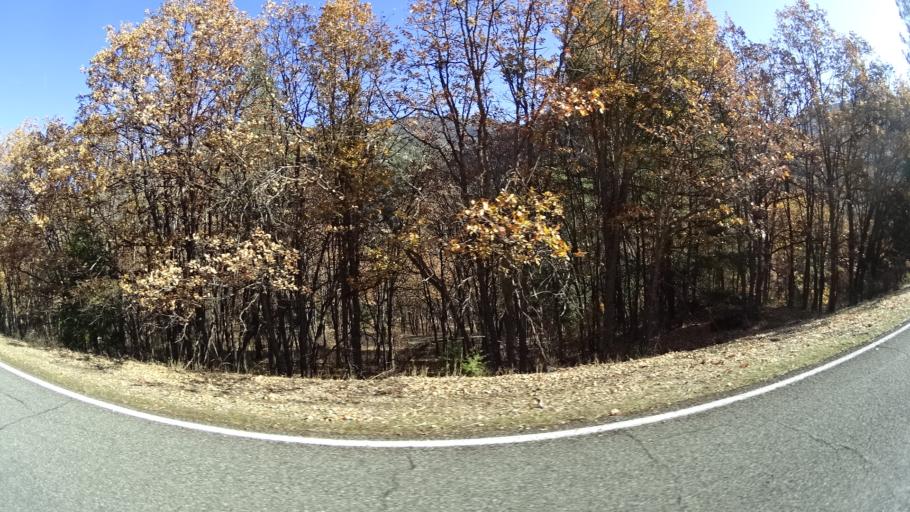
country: US
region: California
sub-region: Siskiyou County
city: Yreka
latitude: 41.9005
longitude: -122.8295
